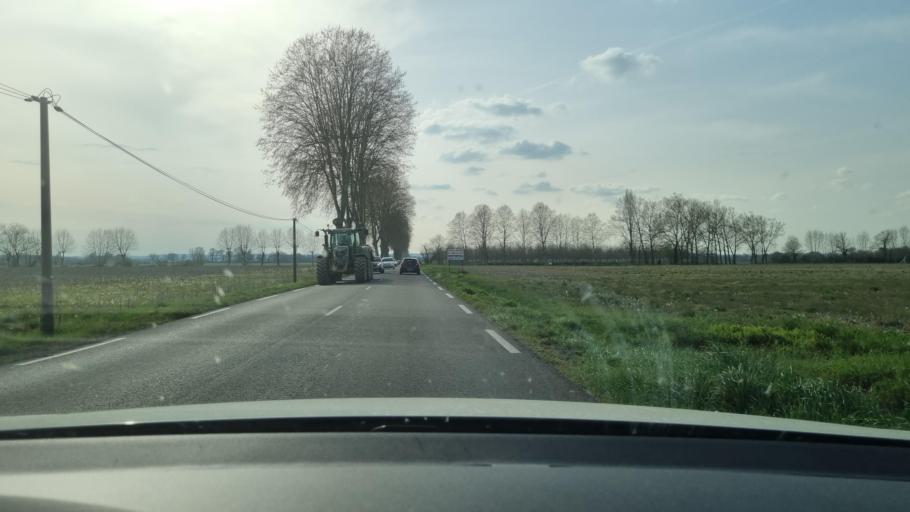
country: FR
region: Midi-Pyrenees
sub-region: Departement des Hautes-Pyrenees
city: Rabastens-de-Bigorre
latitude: 43.3868
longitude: 0.1278
